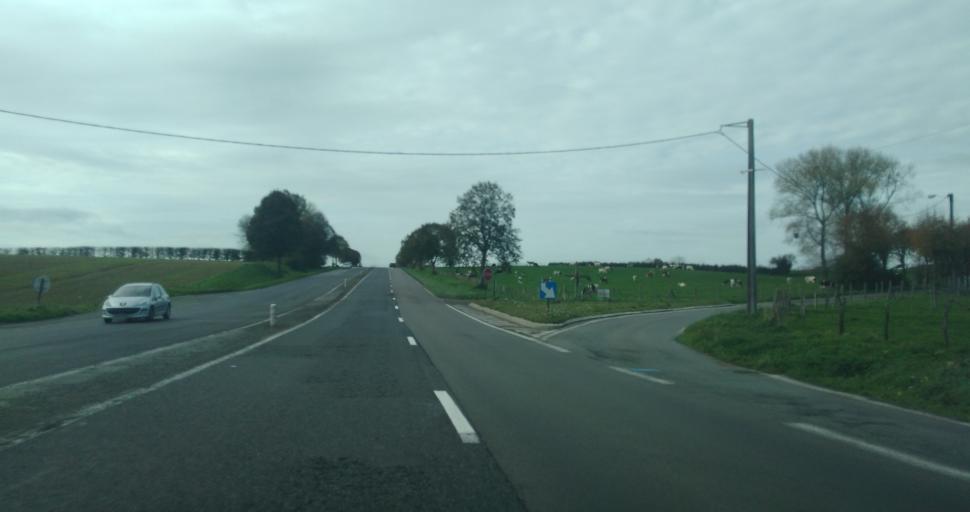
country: FR
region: Nord-Pas-de-Calais
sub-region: Departement du Pas-de-Calais
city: Auchy-les-Hesdin
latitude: 50.3858
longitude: 2.1597
